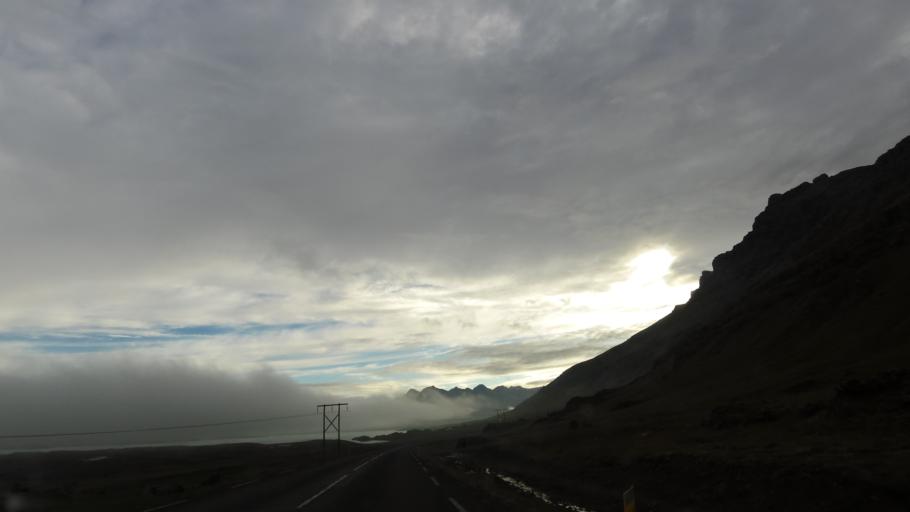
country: IS
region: East
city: Reydarfjoerdur
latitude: 64.5972
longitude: -14.4675
